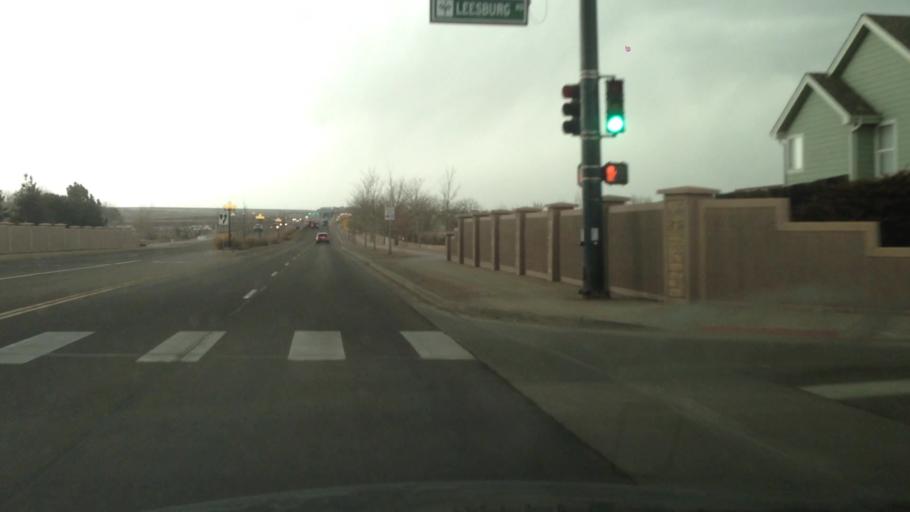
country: US
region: Colorado
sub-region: Douglas County
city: Parker
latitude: 39.4931
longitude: -104.7648
